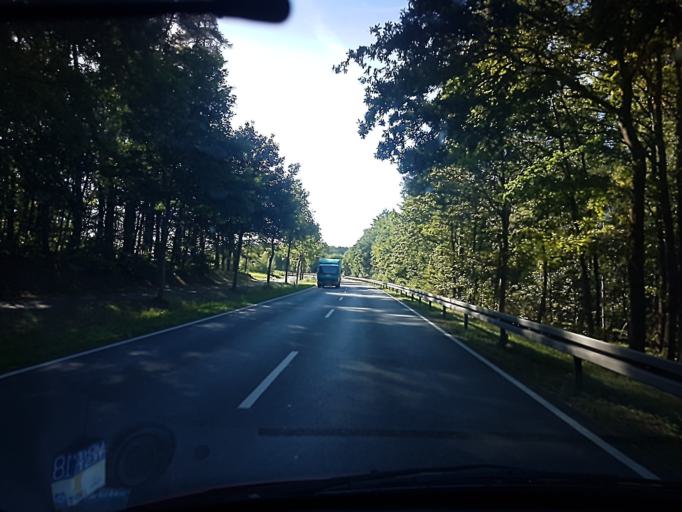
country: DE
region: Bavaria
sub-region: Upper Franconia
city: Heroldsbach
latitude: 49.7091
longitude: 10.9959
